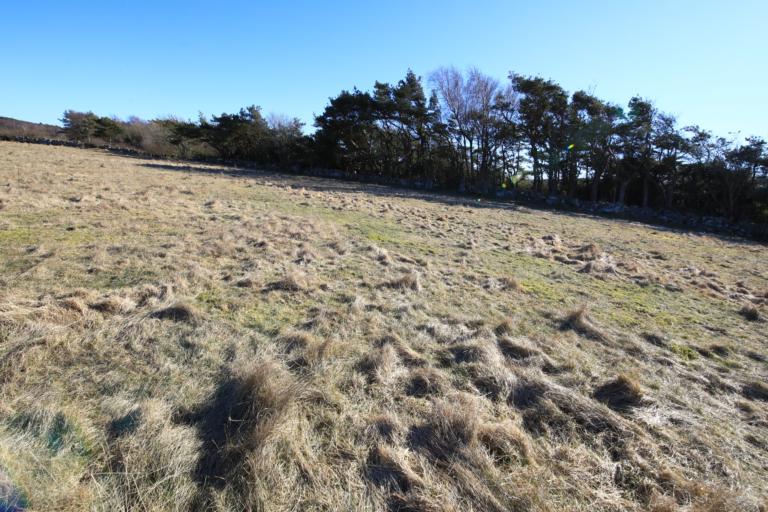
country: SE
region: Halland
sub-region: Kungsbacka Kommun
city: Frillesas
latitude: 57.2256
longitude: 12.1283
